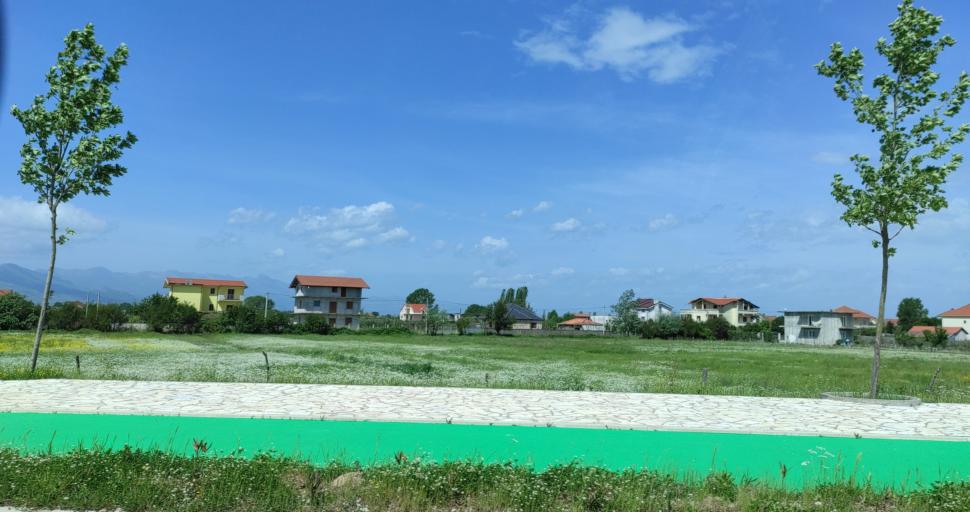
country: AL
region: Shkoder
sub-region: Rrethi i Shkodres
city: Shkoder
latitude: 42.0868
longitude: 19.5043
